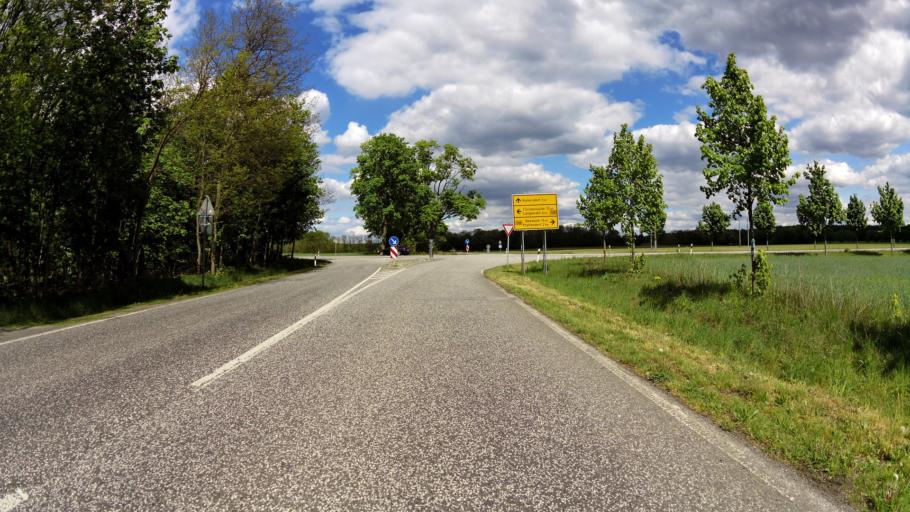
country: DE
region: Brandenburg
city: Rietz Neuendorf
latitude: 52.2817
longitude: 14.1506
